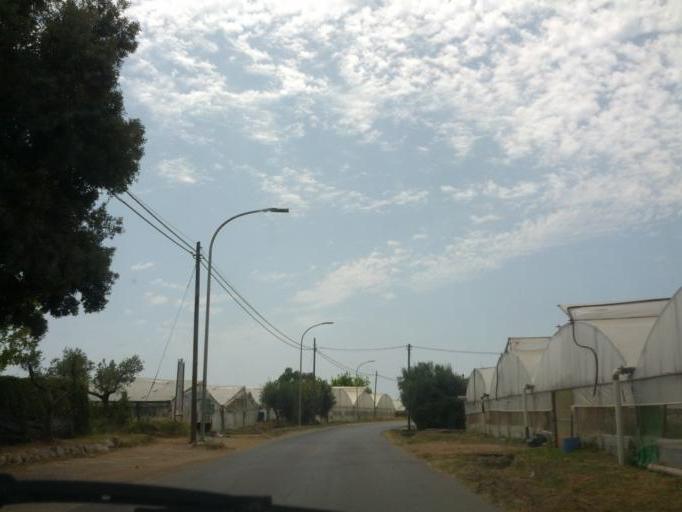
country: IT
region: Latium
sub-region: Provincia di Latina
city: Sperlonga
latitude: 41.2923
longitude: 13.3979
